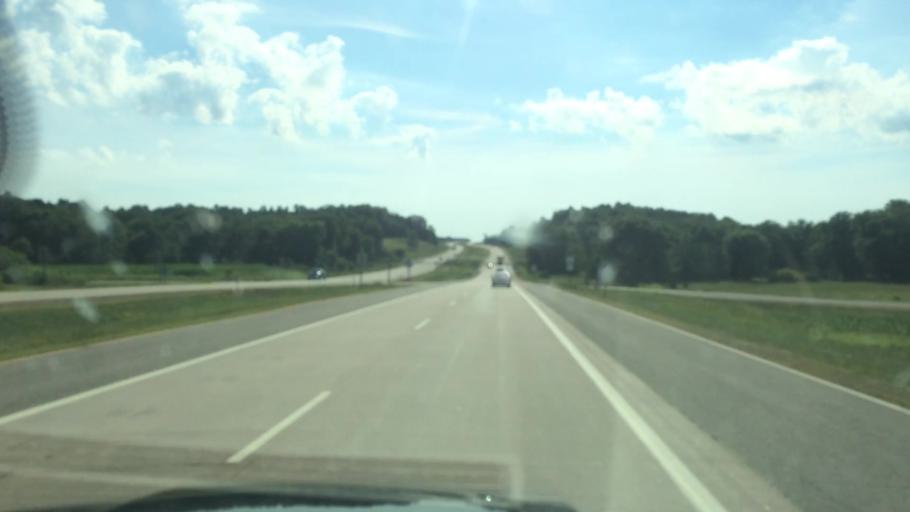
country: US
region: Wisconsin
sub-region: Shawano County
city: Wittenberg
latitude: 44.8036
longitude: -89.0213
